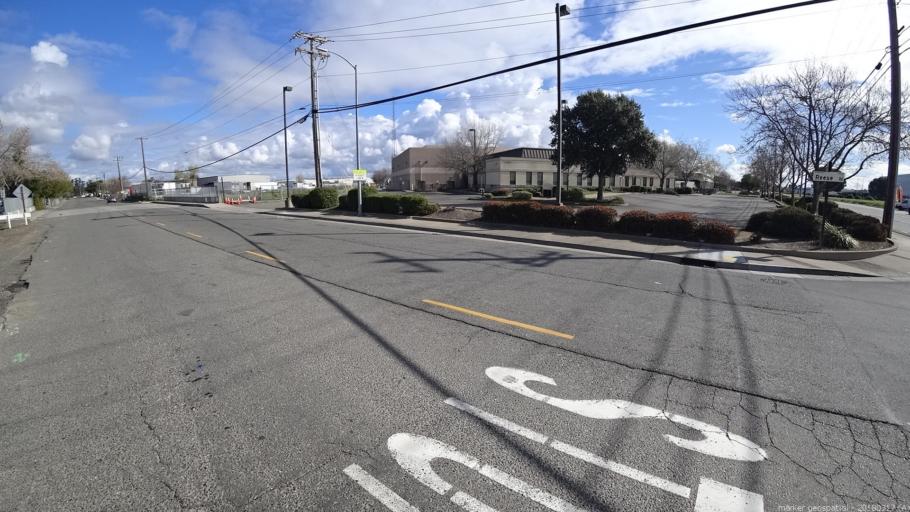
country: US
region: California
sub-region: Sacramento County
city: Florin
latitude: 38.4819
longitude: -121.3962
